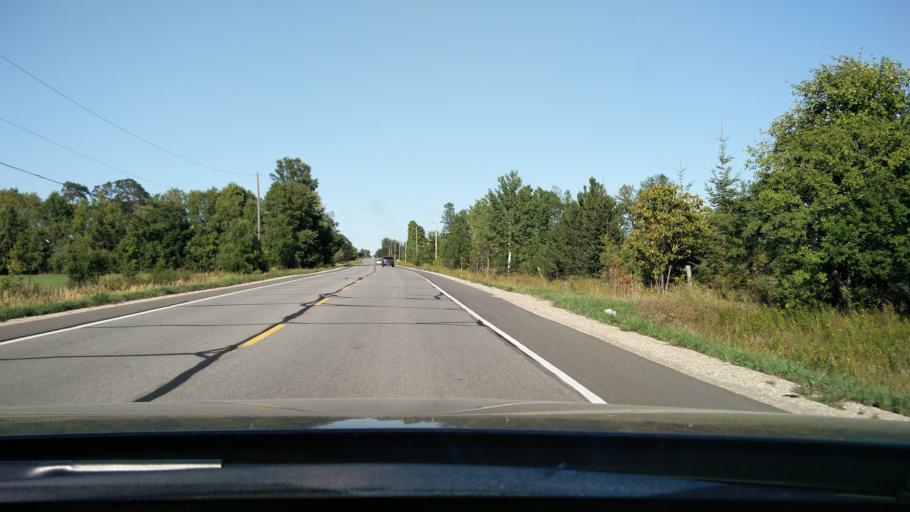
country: CA
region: Ontario
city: Perth
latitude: 44.9597
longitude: -76.1546
